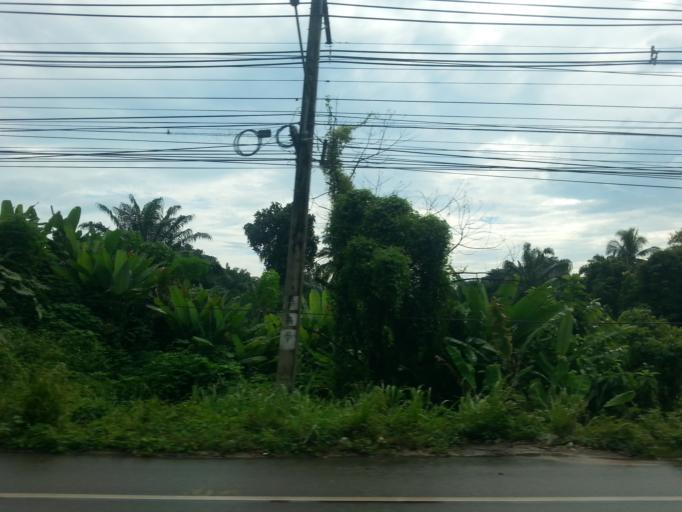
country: TH
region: Krabi
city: Krabi
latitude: 8.0863
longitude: 98.8767
